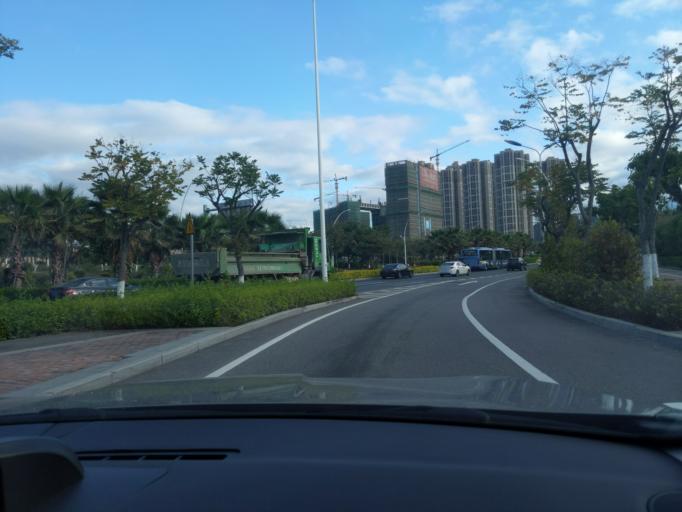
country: CN
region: Fujian
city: Houxi
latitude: 24.6331
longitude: 118.0707
